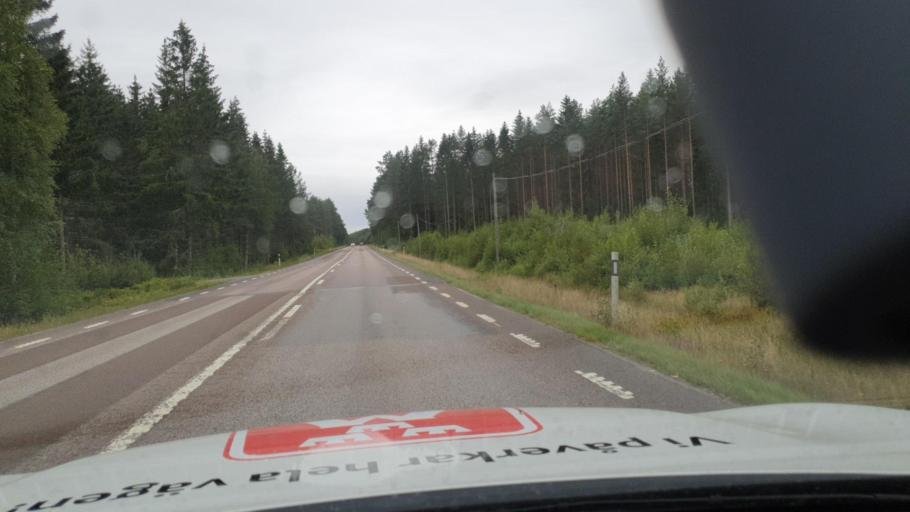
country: SE
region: Vaestra Goetaland
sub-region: Amals Kommun
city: Amal
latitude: 59.0684
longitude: 12.6537
